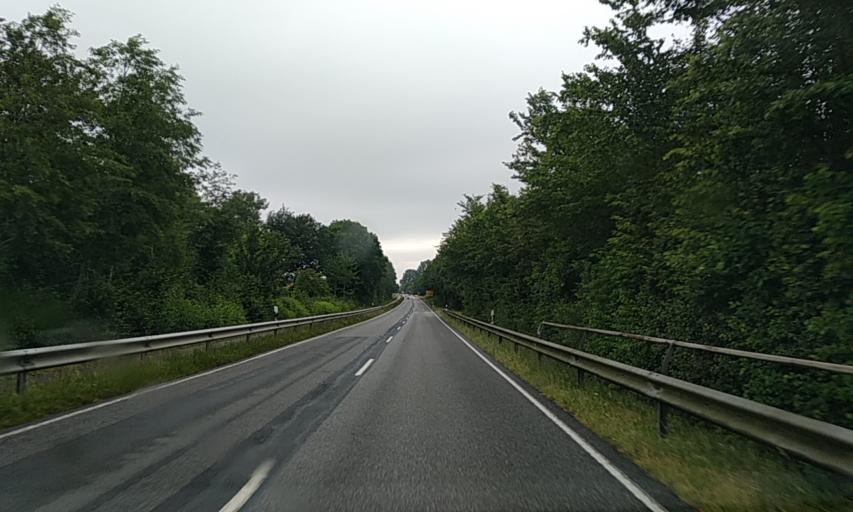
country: DE
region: Schleswig-Holstein
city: Ulsby
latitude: 54.6191
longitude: 9.6192
